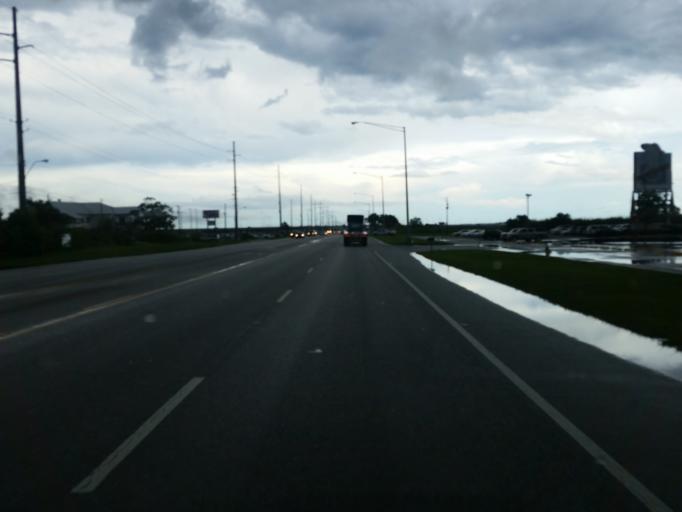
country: US
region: Alabama
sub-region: Mobile County
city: Mobile
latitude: 30.6798
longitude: -87.9978
